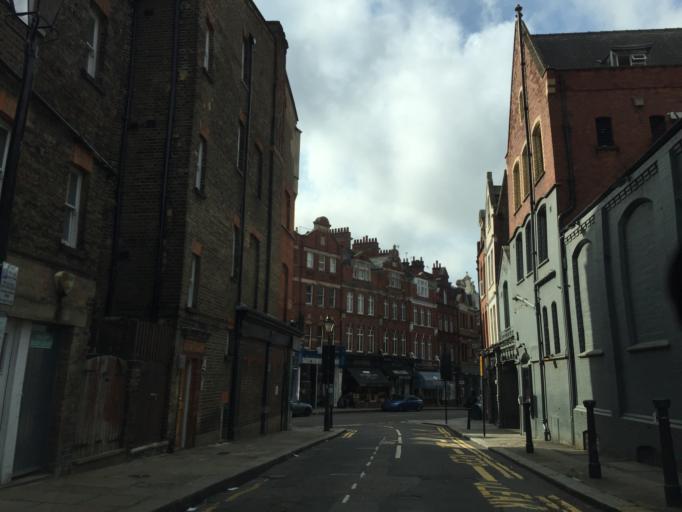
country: GB
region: England
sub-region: Greater London
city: Belsize Park
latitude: 51.5566
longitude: -0.1790
